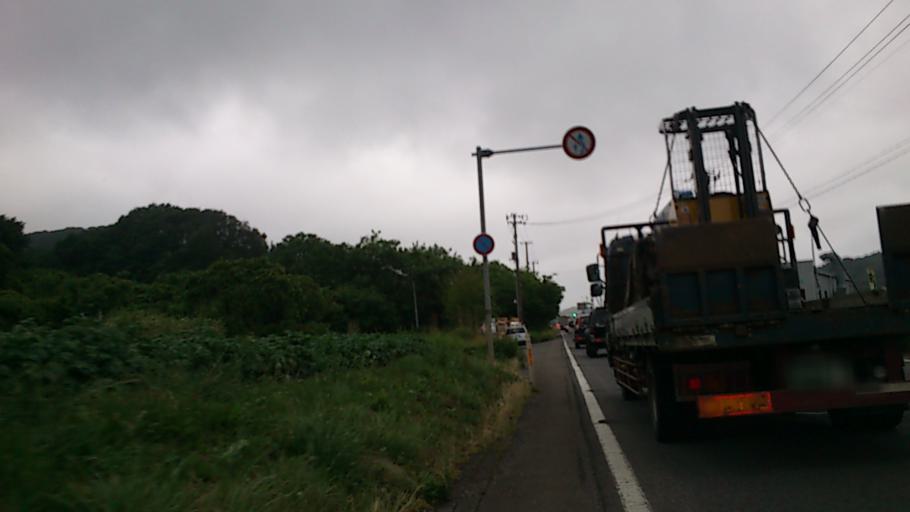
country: JP
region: Fukushima
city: Sukagawa
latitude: 37.1653
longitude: 140.2799
